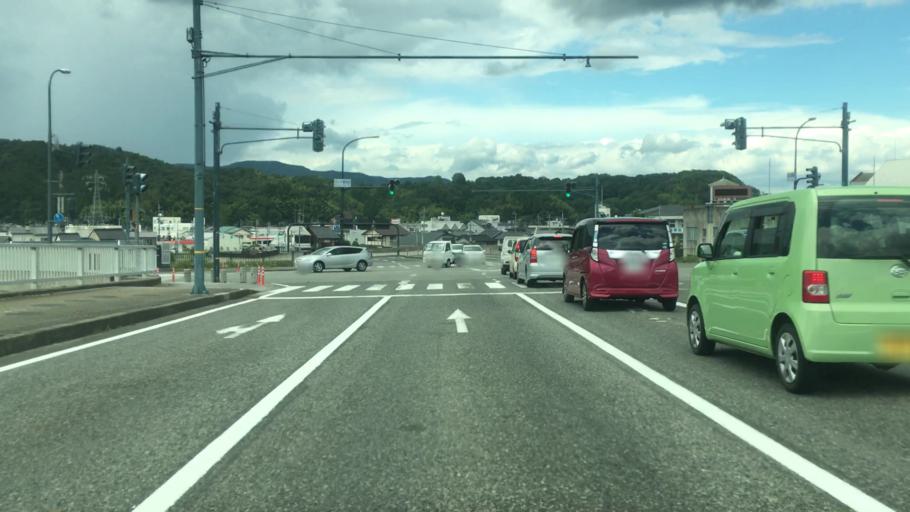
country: JP
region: Hyogo
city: Toyooka
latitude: 35.5276
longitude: 134.8249
